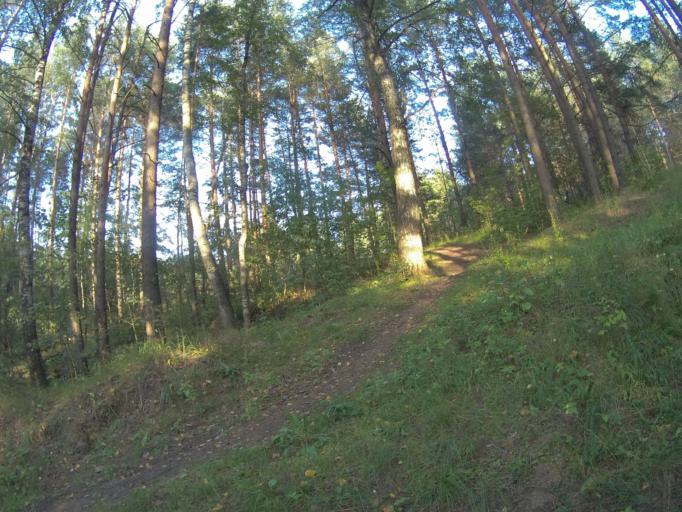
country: RU
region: Vladimir
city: Kommunar
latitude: 56.0690
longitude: 40.4374
